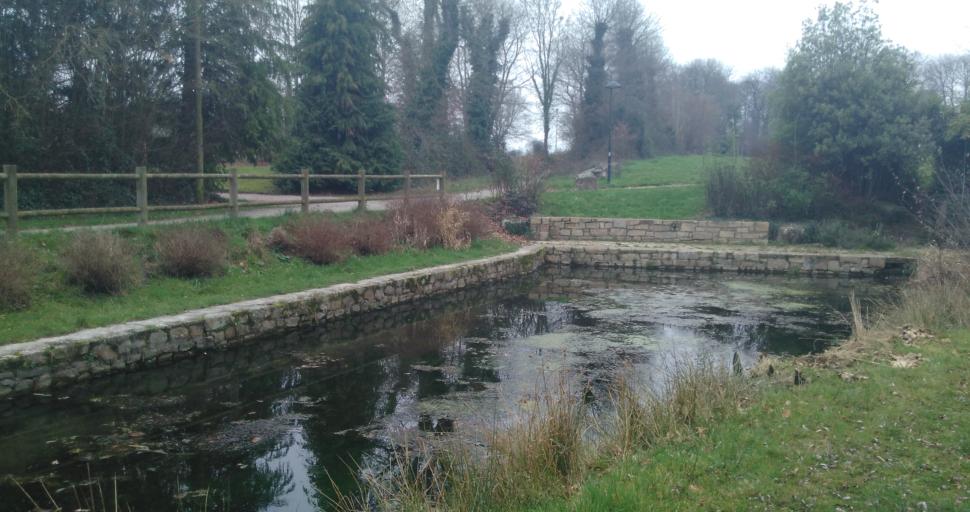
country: FR
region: Brittany
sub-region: Departement d'Ille-et-Vilaine
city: Romille
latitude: 48.2174
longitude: -1.8944
